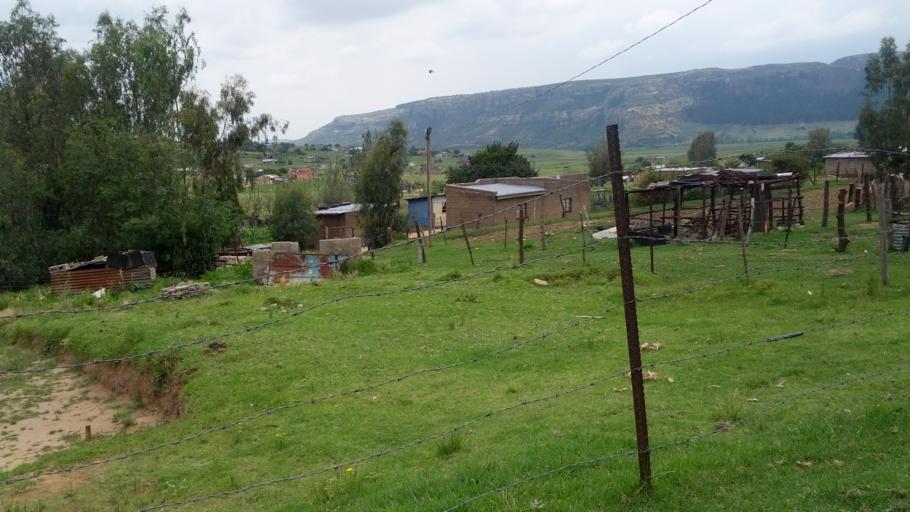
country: LS
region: Leribe
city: Leribe
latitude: -29.0307
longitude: 28.0223
